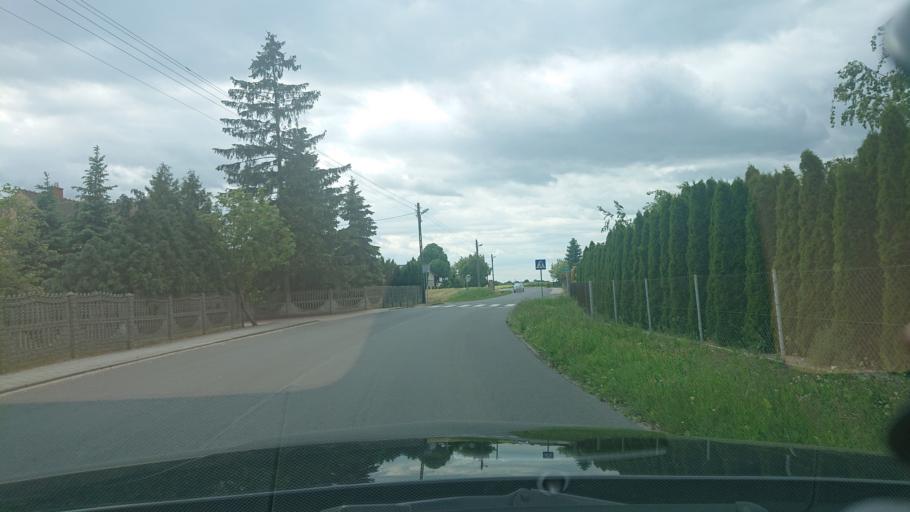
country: PL
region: Greater Poland Voivodeship
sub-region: Powiat gnieznienski
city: Gniezno
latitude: 52.5419
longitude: 17.5631
